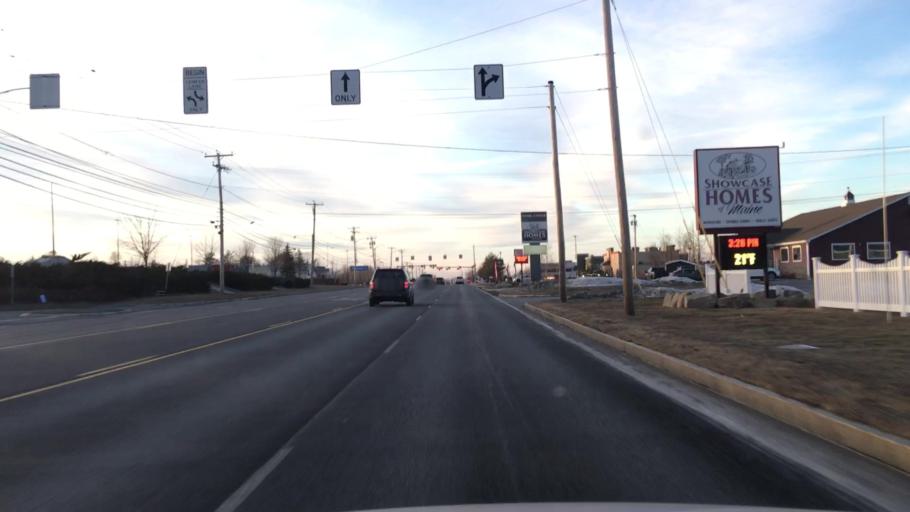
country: US
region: Maine
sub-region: Penobscot County
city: Brewer
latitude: 44.7751
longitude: -68.7303
